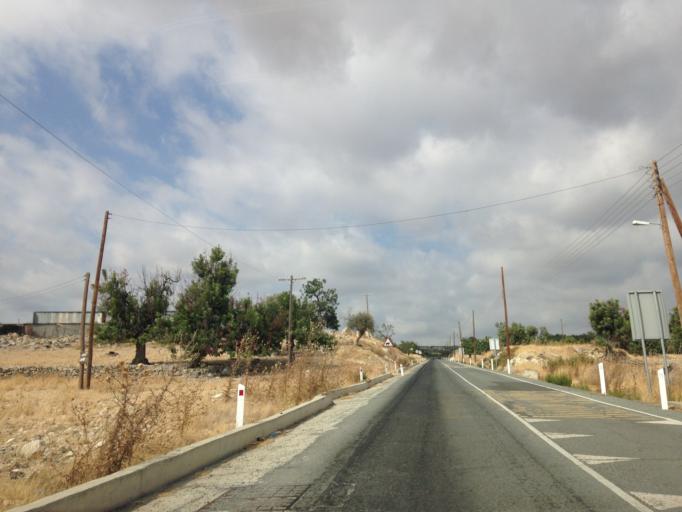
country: CY
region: Limassol
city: Pissouri
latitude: 34.7008
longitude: 32.7632
